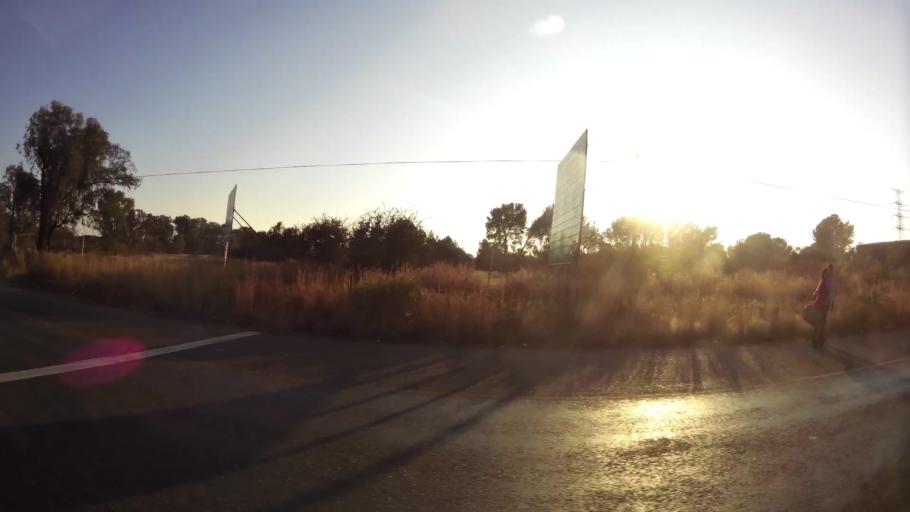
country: ZA
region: Orange Free State
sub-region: Mangaung Metropolitan Municipality
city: Bloemfontein
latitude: -29.0805
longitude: 26.1566
